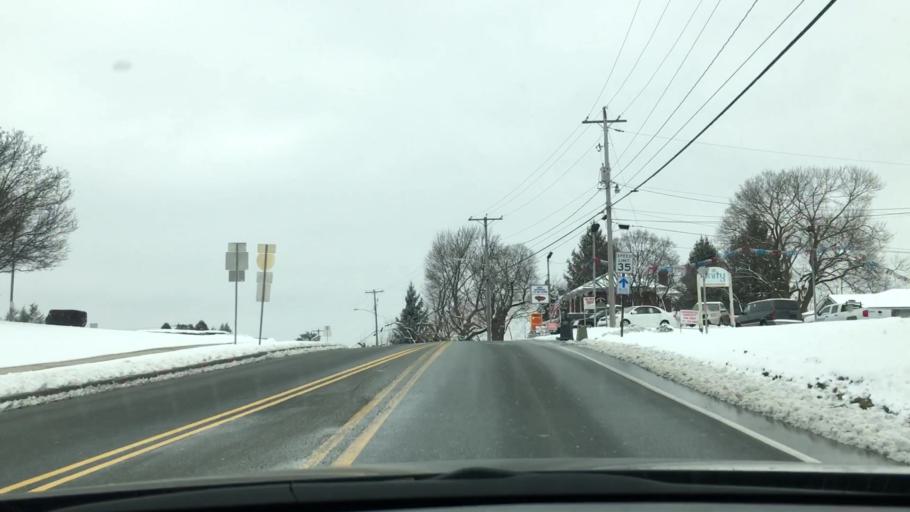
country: US
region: Pennsylvania
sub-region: York County
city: Spry
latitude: 39.9123
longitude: -76.6824
